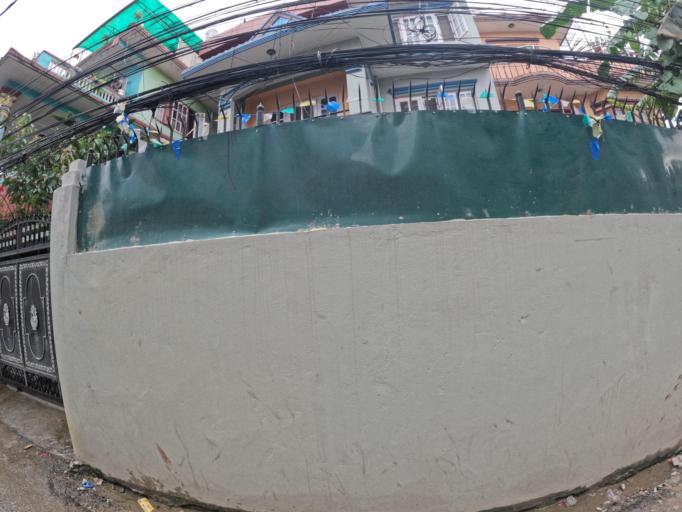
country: NP
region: Central Region
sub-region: Bagmati Zone
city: Kathmandu
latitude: 27.7466
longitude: 85.3225
